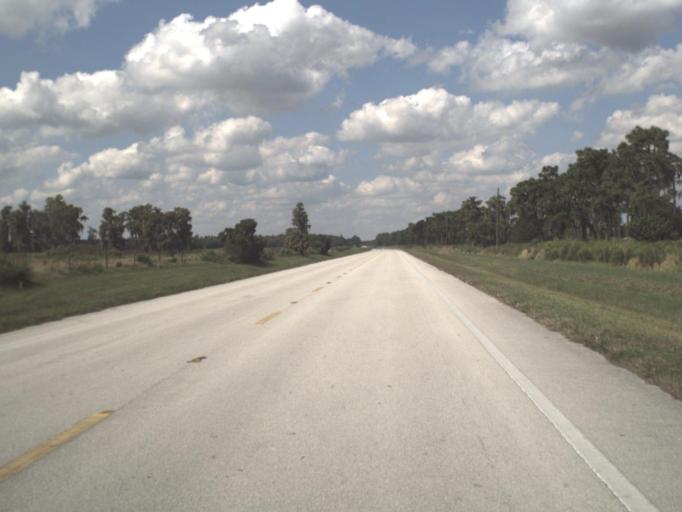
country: US
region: Florida
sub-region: Highlands County
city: Sebring
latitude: 27.4417
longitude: -81.6146
